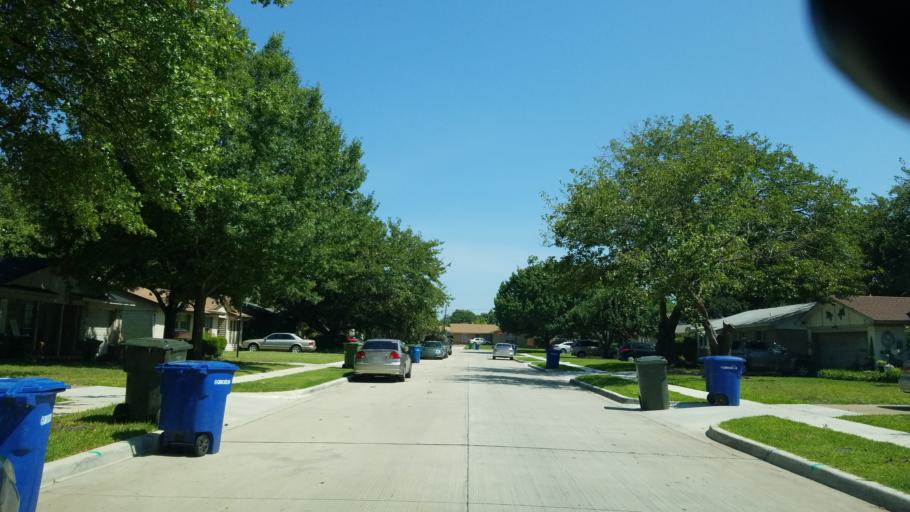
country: US
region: Texas
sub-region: Dallas County
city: Carrollton
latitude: 32.9699
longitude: -96.9053
